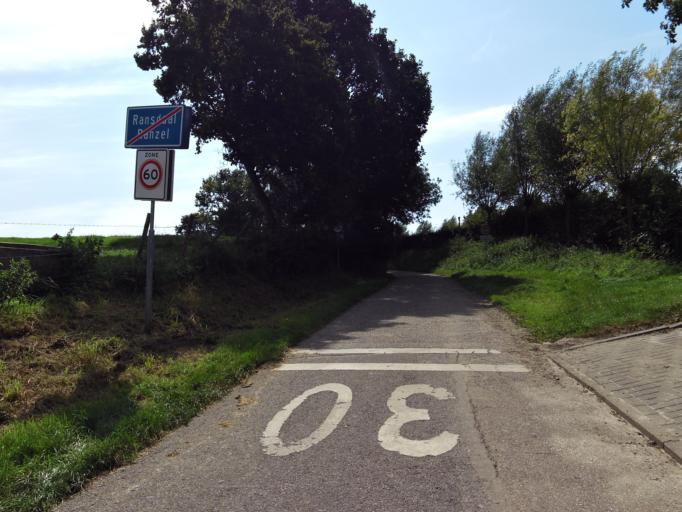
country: NL
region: Limburg
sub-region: Gemeente Voerendaal
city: Klimmen
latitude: 50.8653
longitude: 5.9005
